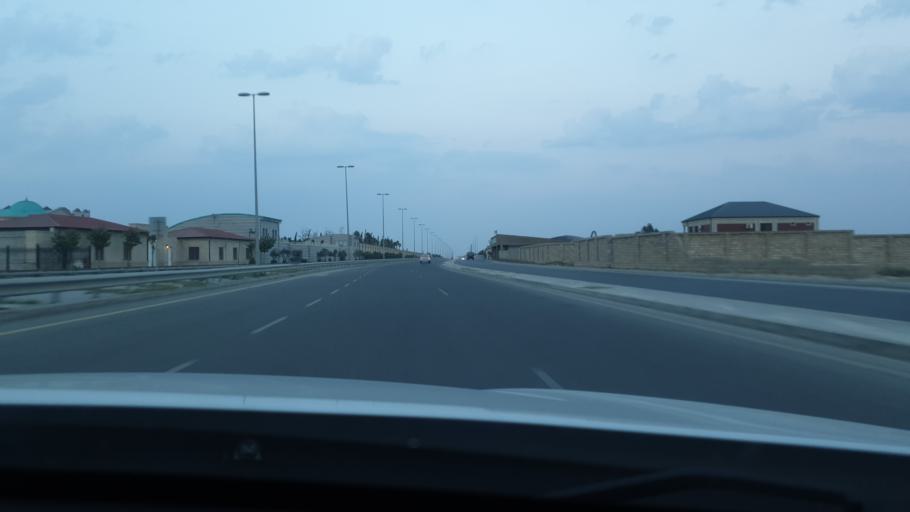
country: AZ
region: Baki
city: Nardaran
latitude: 40.5828
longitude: 50.0121
